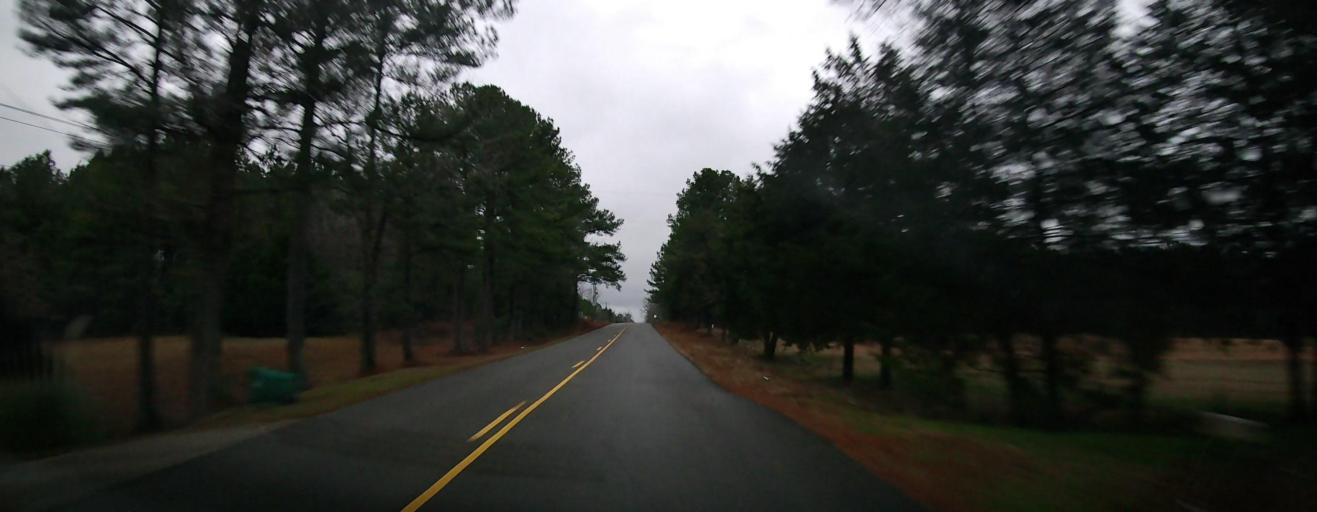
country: US
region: Alabama
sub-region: Tuscaloosa County
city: Vance
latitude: 33.1407
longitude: -87.2298
